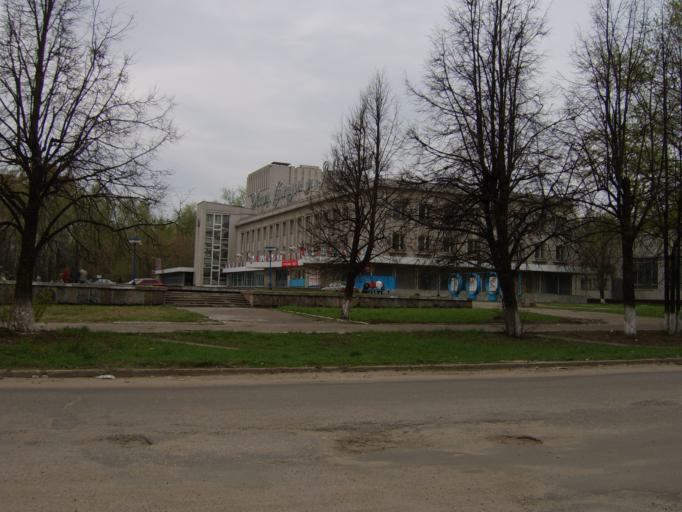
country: RU
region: Mariy-El
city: Yoshkar-Ola
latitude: 56.6390
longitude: 47.8712
